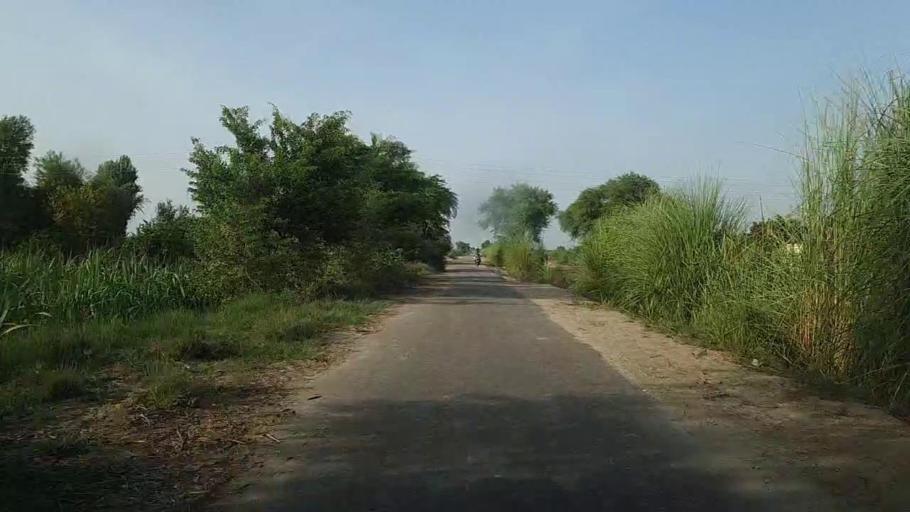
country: PK
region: Sindh
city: Ubauro
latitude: 28.0970
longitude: 69.8223
